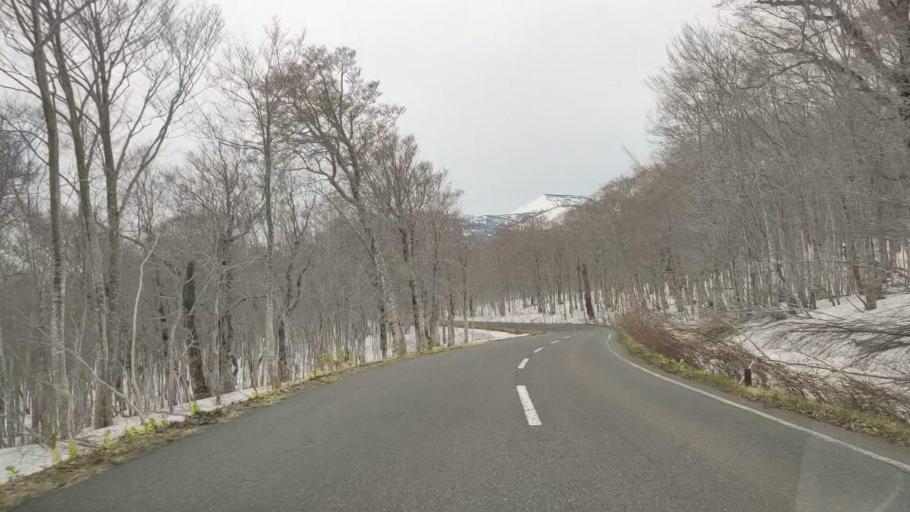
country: JP
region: Aomori
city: Aomori Shi
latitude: 40.6390
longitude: 140.9319
